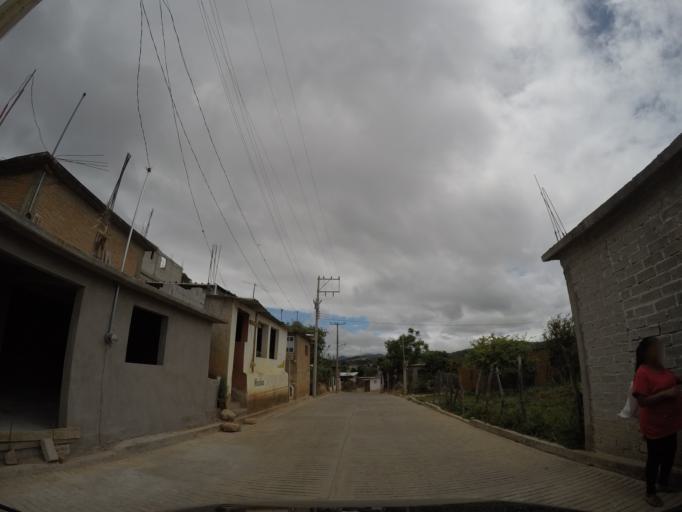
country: MX
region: Oaxaca
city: San Lorenzo Albarradas
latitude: 16.9053
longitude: -96.2611
